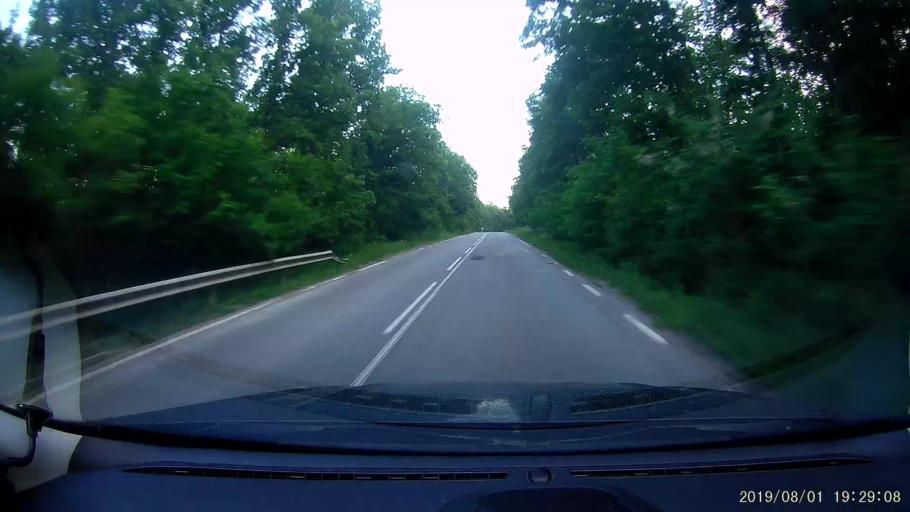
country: BG
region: Burgas
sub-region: Obshtina Sungurlare
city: Sungurlare
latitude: 42.8311
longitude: 26.9103
